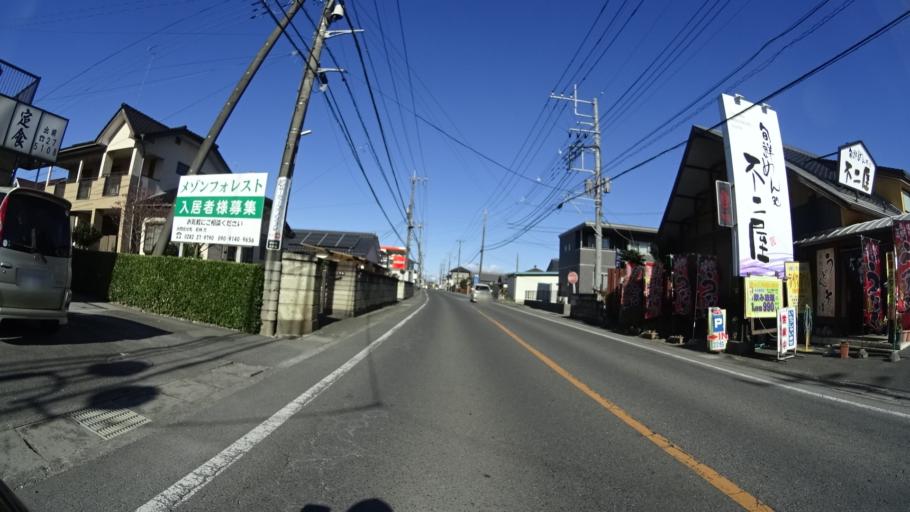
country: JP
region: Tochigi
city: Tochigi
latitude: 36.4077
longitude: 139.7443
